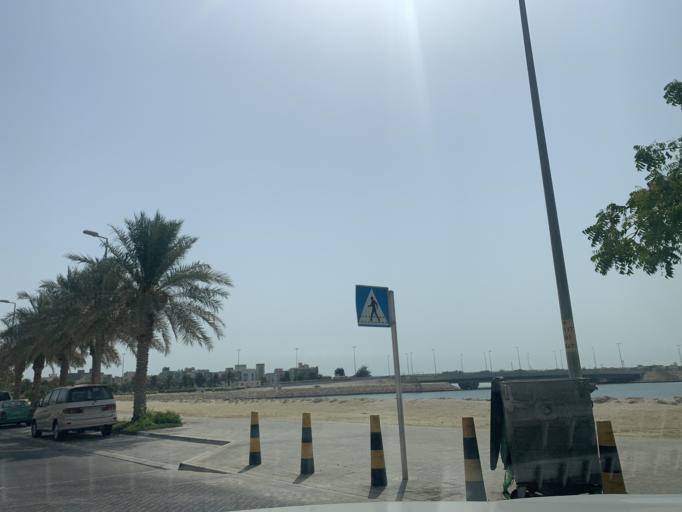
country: BH
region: Manama
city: Jidd Hafs
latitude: 26.2242
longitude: 50.4499
